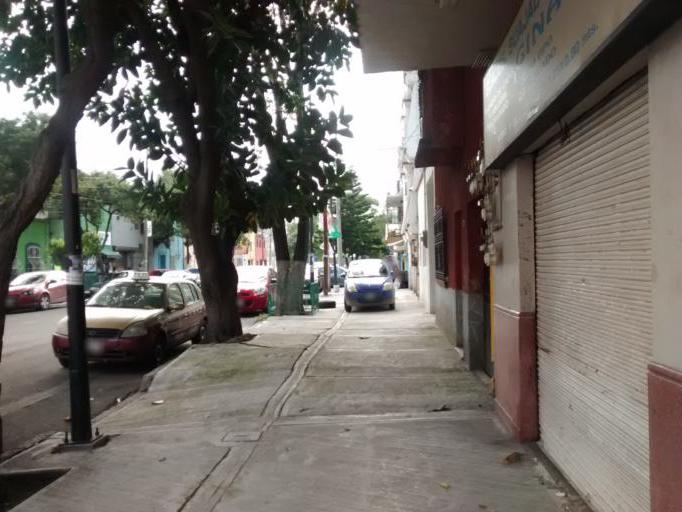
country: MX
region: Mexico City
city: Benito Juarez
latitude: 19.4085
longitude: -99.1407
